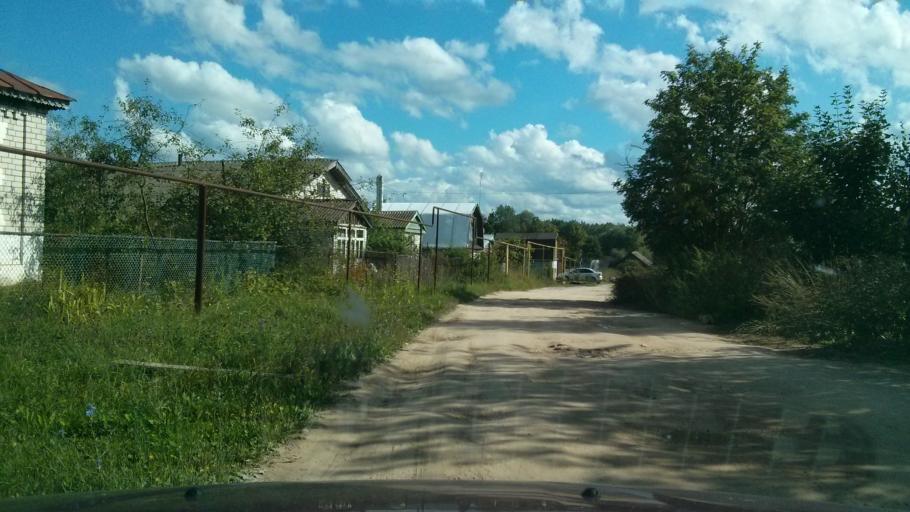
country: RU
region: Nizjnij Novgorod
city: Vacha
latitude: 55.7579
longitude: 42.5171
